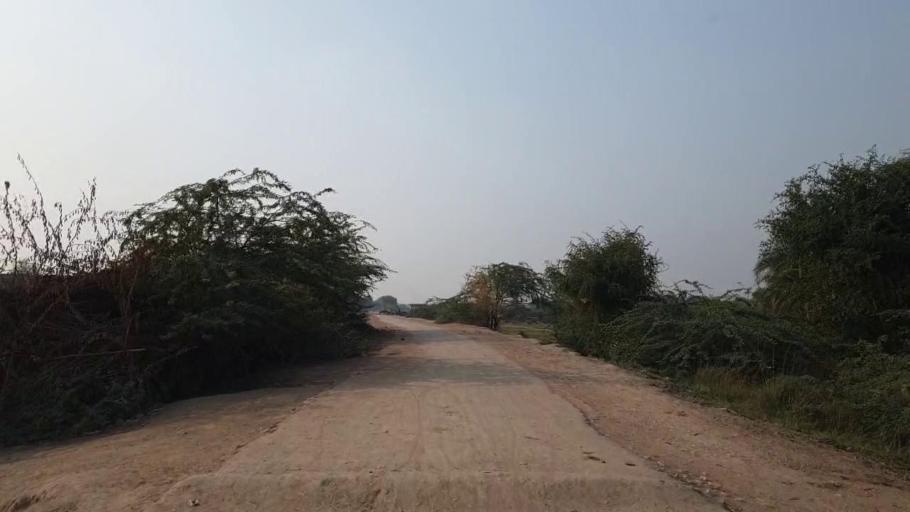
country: PK
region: Sindh
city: Bhan
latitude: 26.5590
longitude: 67.7102
